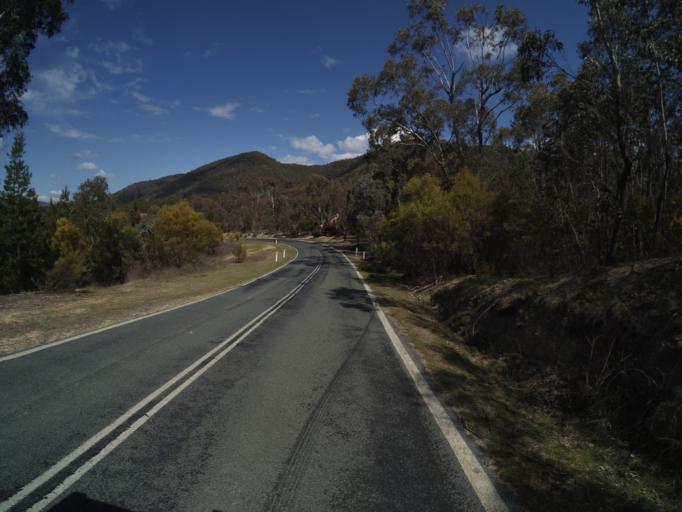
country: AU
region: Australian Capital Territory
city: Macquarie
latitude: -35.3587
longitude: 148.9464
